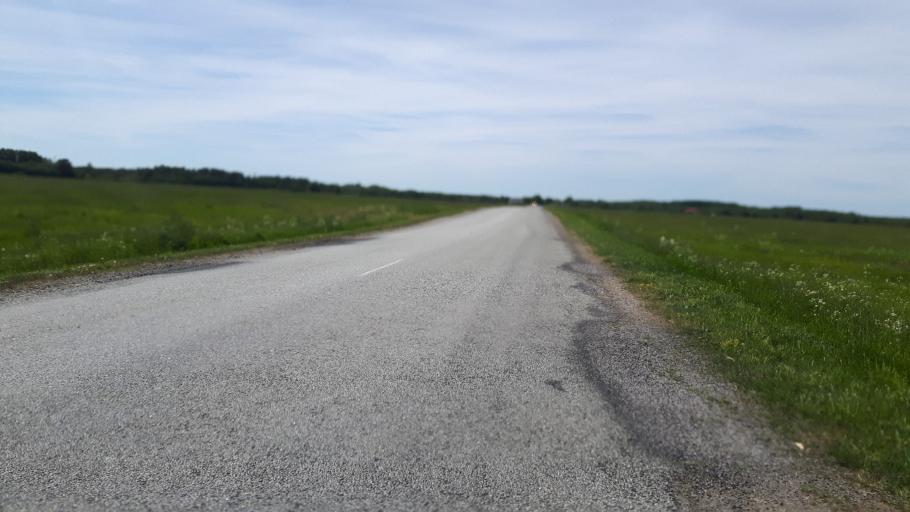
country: EE
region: Harju
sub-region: Kuusalu vald
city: Kuusalu
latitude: 59.4633
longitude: 25.3314
